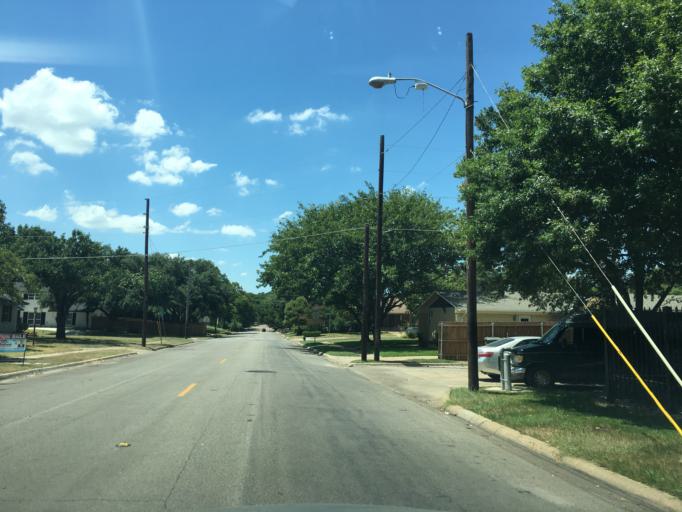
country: US
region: Texas
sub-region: Dallas County
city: Garland
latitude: 32.8500
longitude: -96.6892
